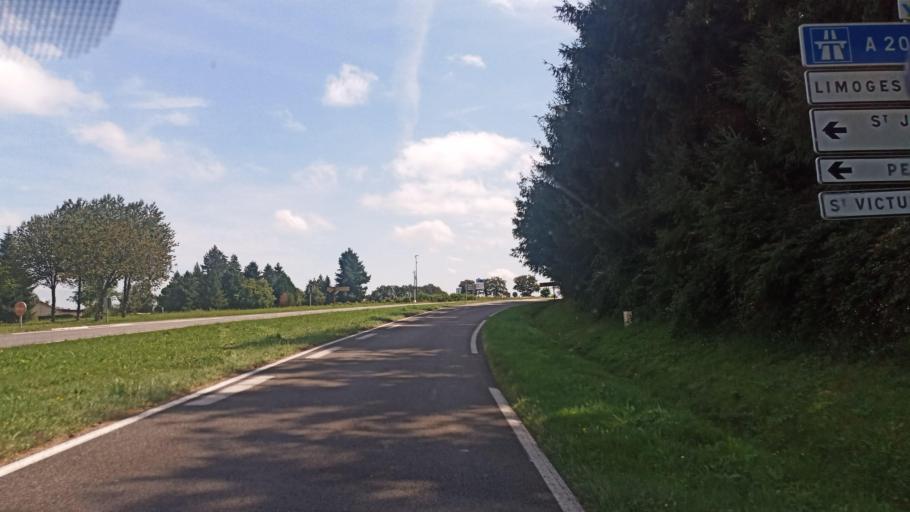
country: FR
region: Limousin
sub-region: Departement de la Haute-Vienne
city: Oradour-sur-Glane
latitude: 45.9256
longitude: 1.0426
